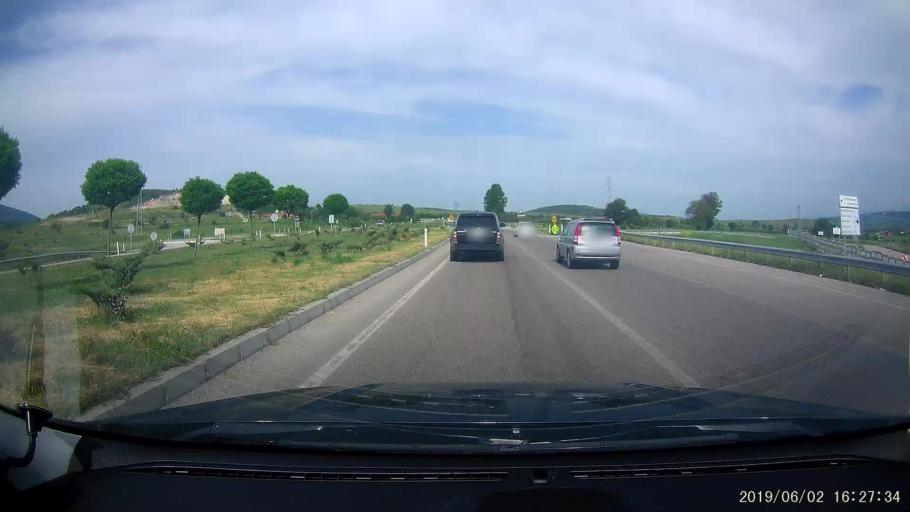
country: TR
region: Samsun
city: Ladik
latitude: 41.0020
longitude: 35.8301
